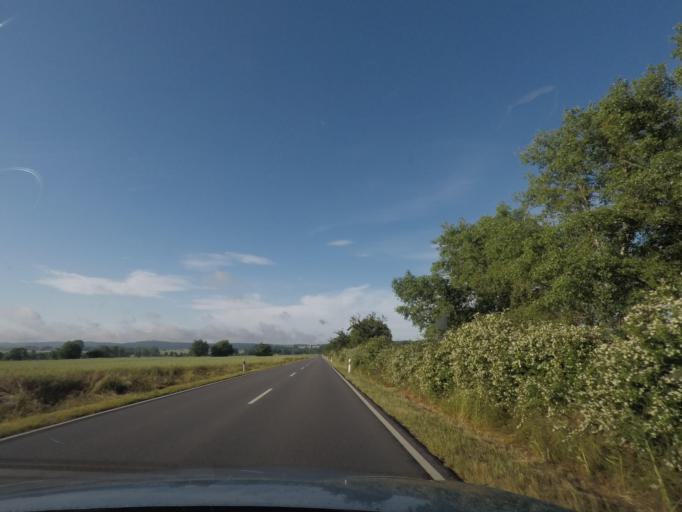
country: DE
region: Saxony-Anhalt
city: Huy-Neinstedt
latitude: 51.9978
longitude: 10.8943
